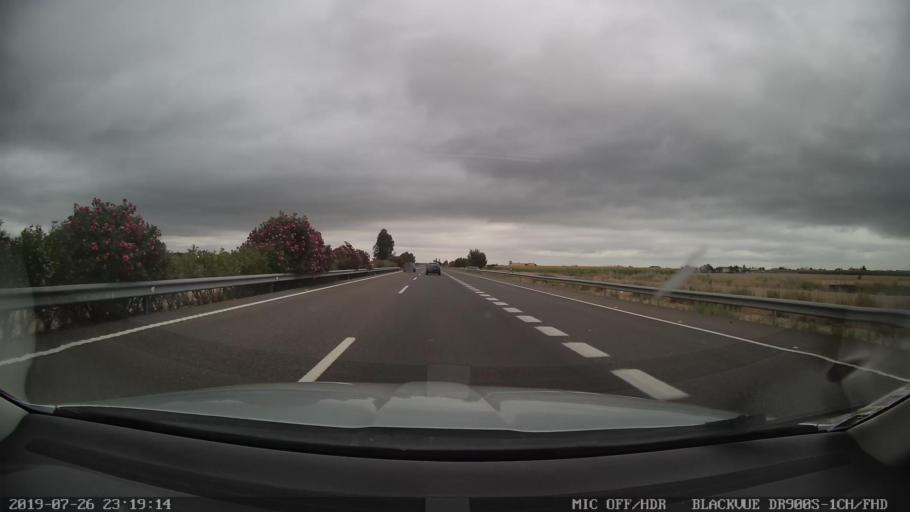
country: ES
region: Extremadura
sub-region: Provincia de Caceres
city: Almoharin
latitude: 39.1051
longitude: -5.9962
